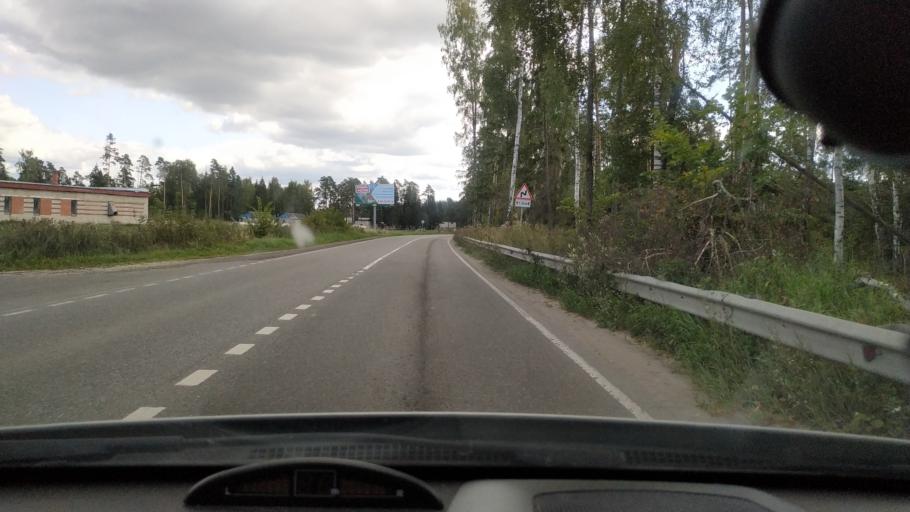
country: RU
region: Moskovskaya
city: Zheleznodorozhnyy
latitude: 55.7941
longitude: 38.0329
